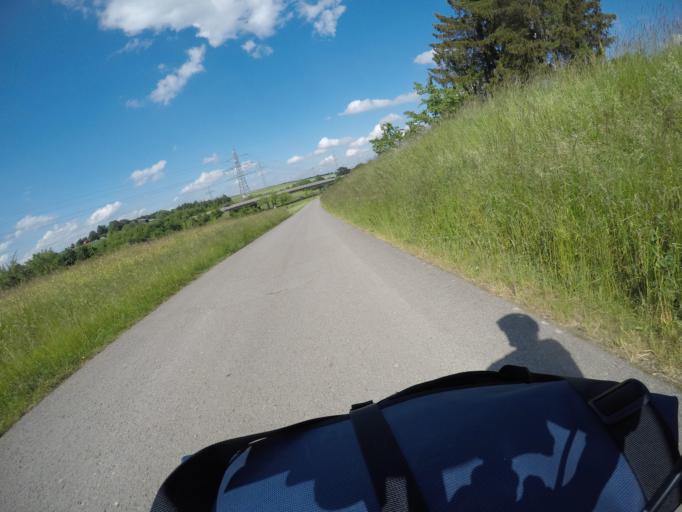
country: DE
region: Baden-Wuerttemberg
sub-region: Regierungsbezirk Stuttgart
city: Herrenberg
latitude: 48.6172
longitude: 8.8454
